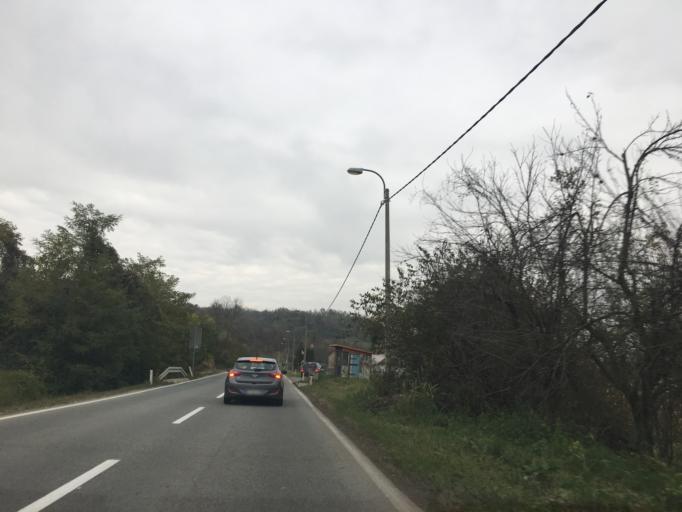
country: RS
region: Central Serbia
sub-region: Raski Okrug
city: Kraljevo
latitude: 43.7184
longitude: 20.7796
